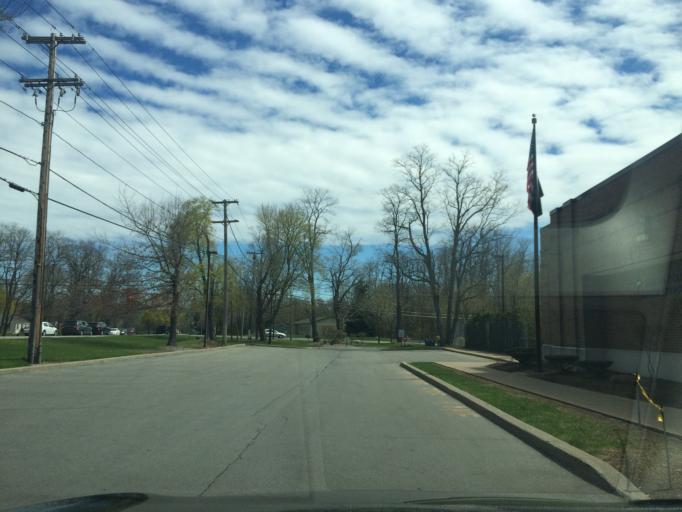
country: US
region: New York
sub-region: Monroe County
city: Pittsford
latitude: 43.0813
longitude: -77.4954
